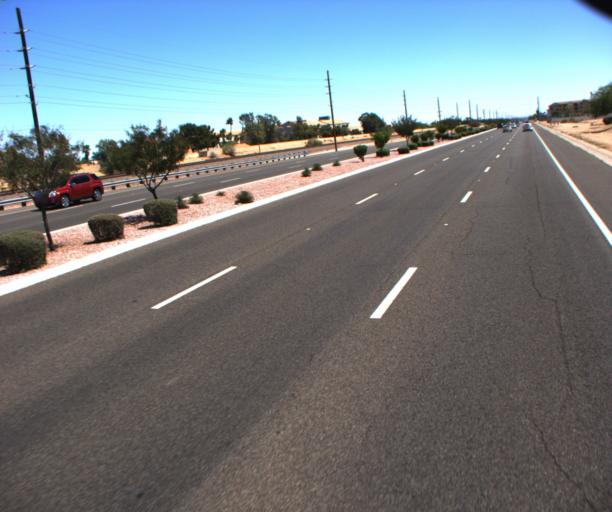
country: US
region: Arizona
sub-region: Maricopa County
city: Sun City West
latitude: 33.6637
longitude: -112.3826
